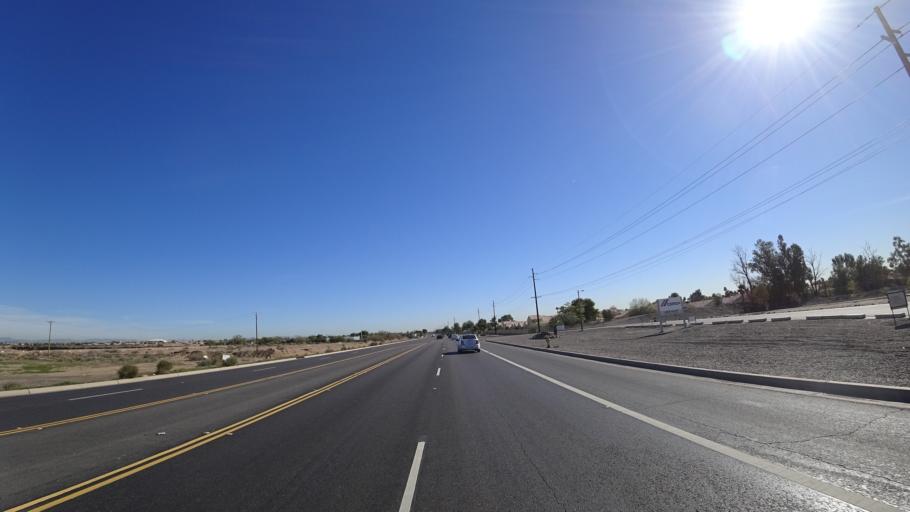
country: US
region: Arizona
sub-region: Maricopa County
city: Litchfield Park
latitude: 33.4930
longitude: -112.3099
